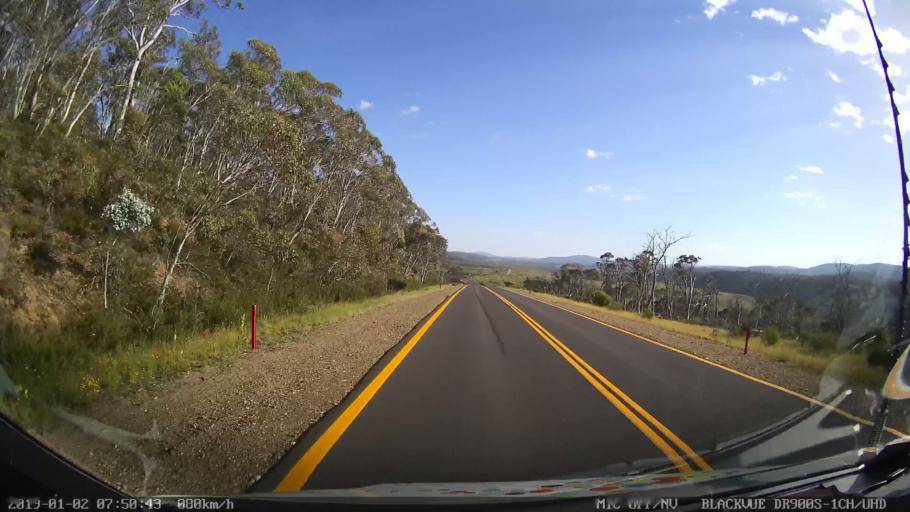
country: AU
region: New South Wales
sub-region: Tumut Shire
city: Tumut
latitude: -35.7271
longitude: 148.5286
